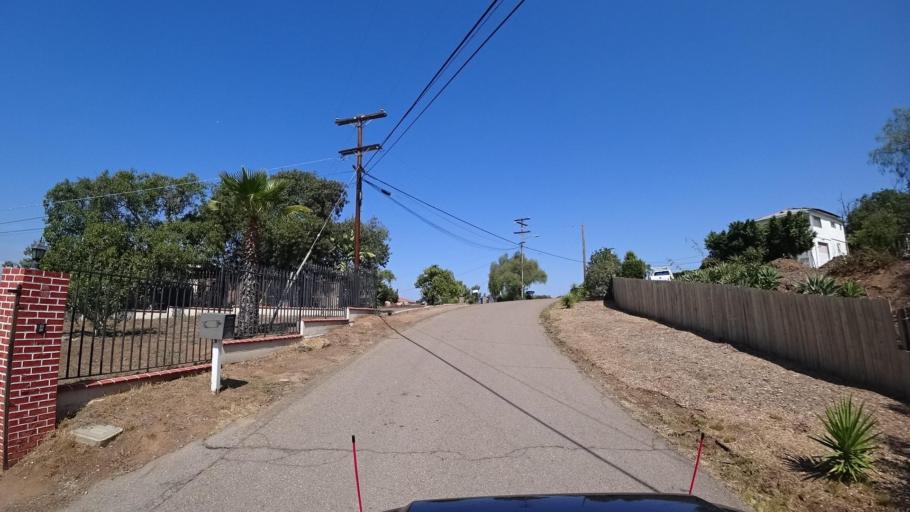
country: US
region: California
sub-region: San Diego County
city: Spring Valley
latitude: 32.7352
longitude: -116.9978
